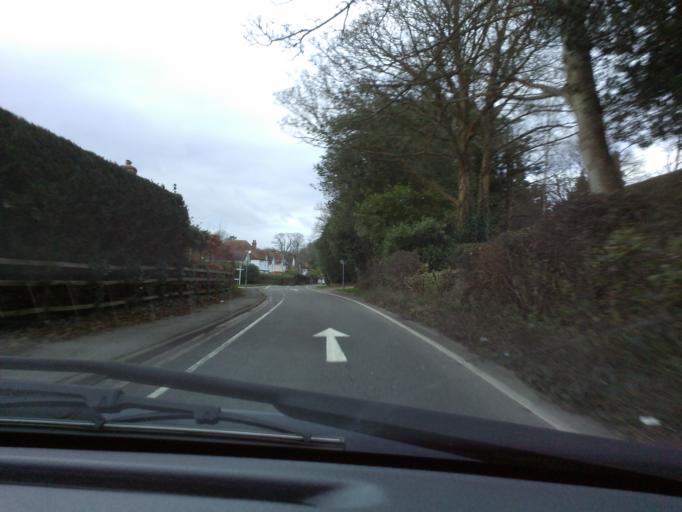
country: GB
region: England
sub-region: Hampshire
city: Lyndhurst
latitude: 50.8687
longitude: -1.5790
